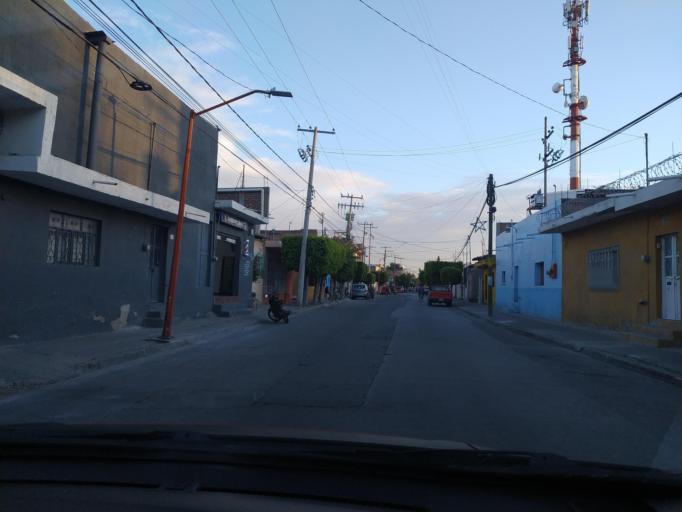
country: MX
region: Guanajuato
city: San Francisco del Rincon
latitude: 21.0086
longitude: -101.8546
